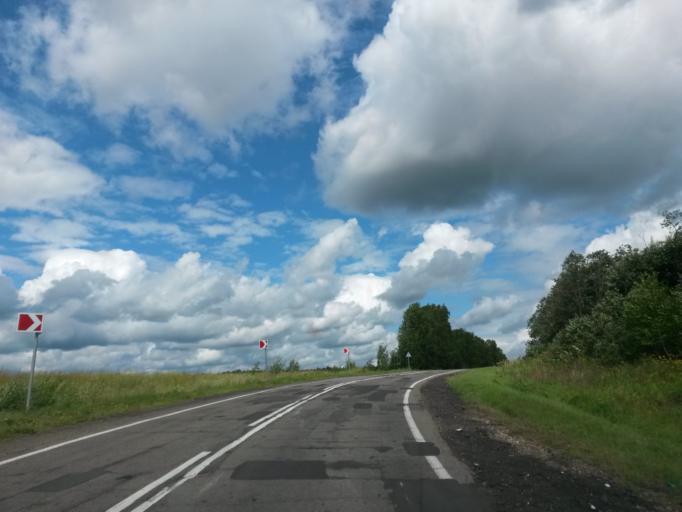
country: RU
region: Jaroslavl
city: Tutayev
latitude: 57.9427
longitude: 39.4955
